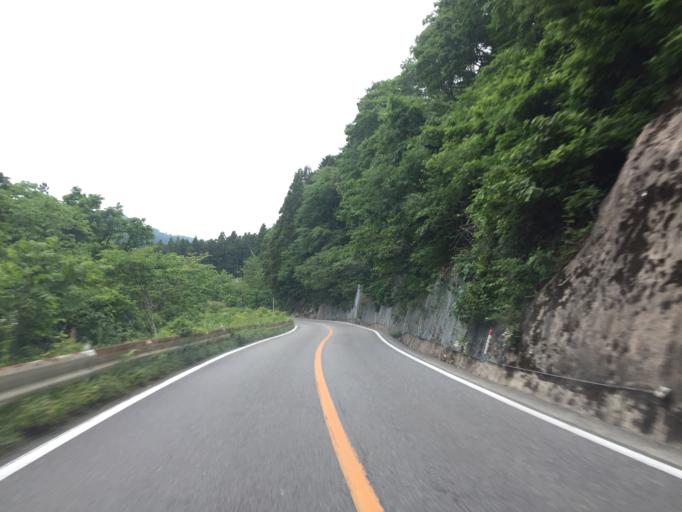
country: JP
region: Fukushima
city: Namie
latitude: 37.4139
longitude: 140.9270
